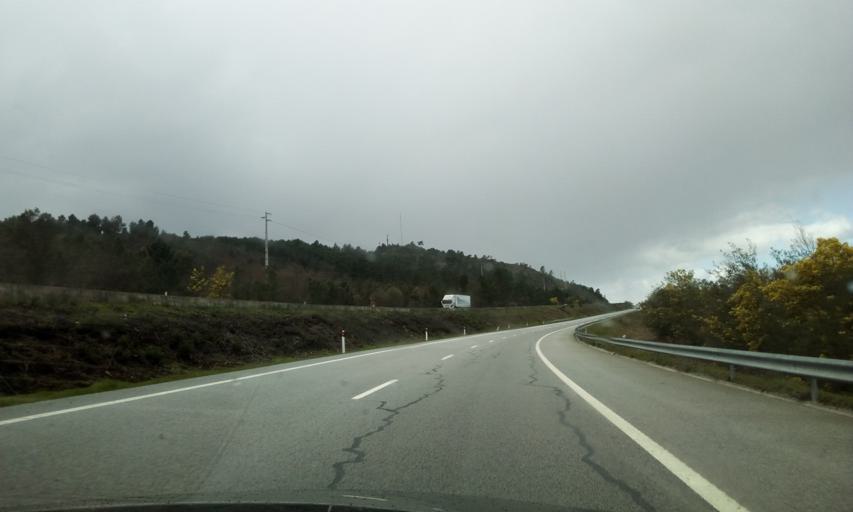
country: PT
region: Viseu
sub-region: Mangualde
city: Mangualde
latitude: 40.6162
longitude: -7.7259
